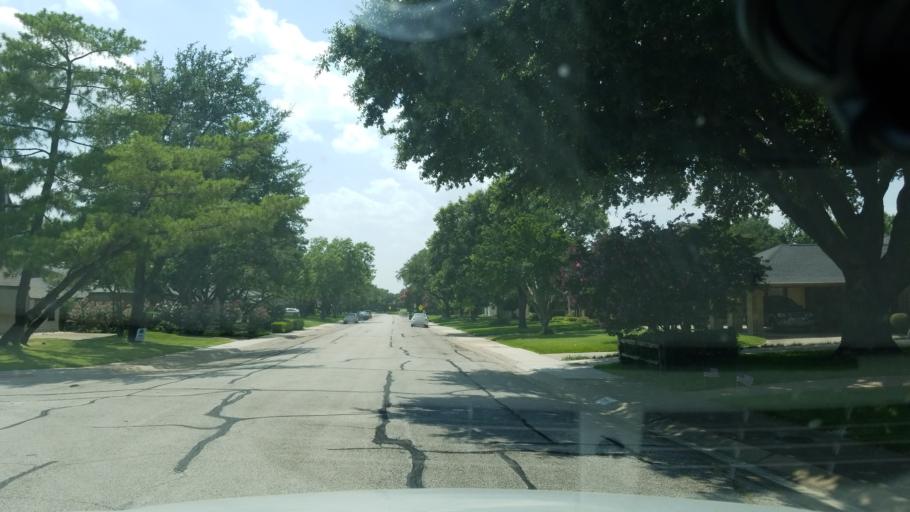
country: US
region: Texas
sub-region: Dallas County
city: Addison
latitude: 32.9675
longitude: -96.8599
